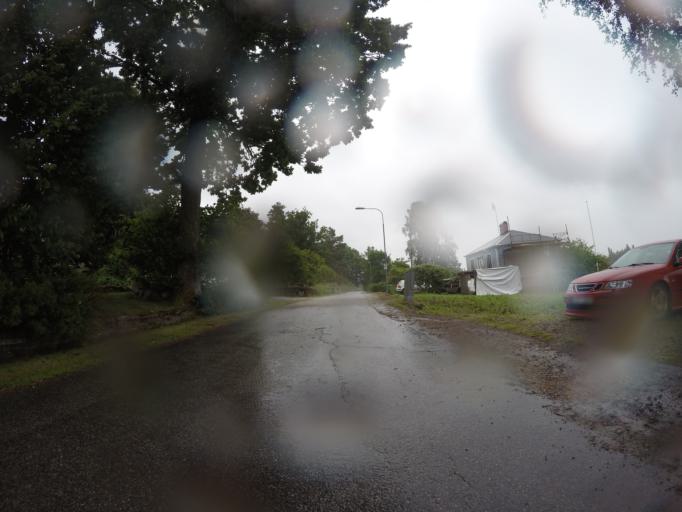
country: SE
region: Vaestra Goetaland
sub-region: Trollhattan
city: Sjuntorp
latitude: 58.1614
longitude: 12.3040
